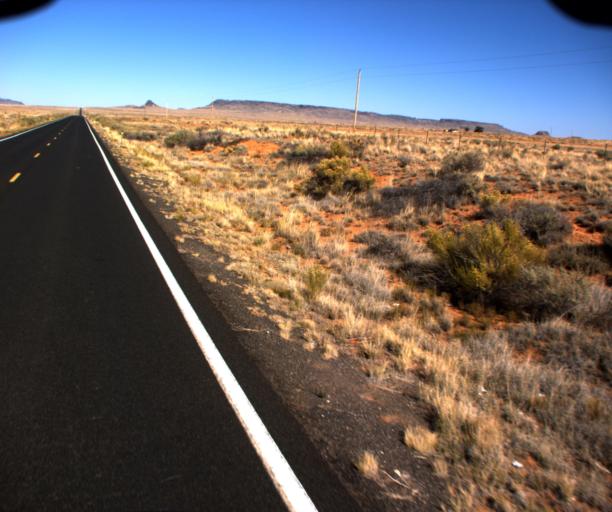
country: US
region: Arizona
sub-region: Navajo County
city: Dilkon
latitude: 35.3395
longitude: -110.4238
